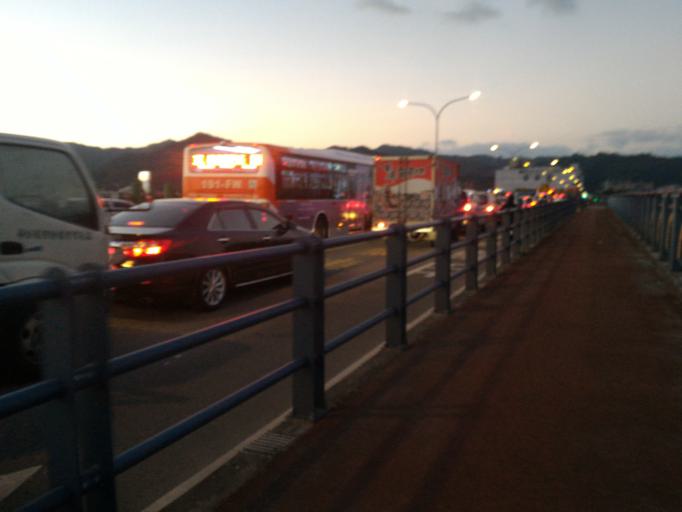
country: TW
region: Taipei
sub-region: Taipei
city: Banqiao
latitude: 24.9660
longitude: 121.4047
